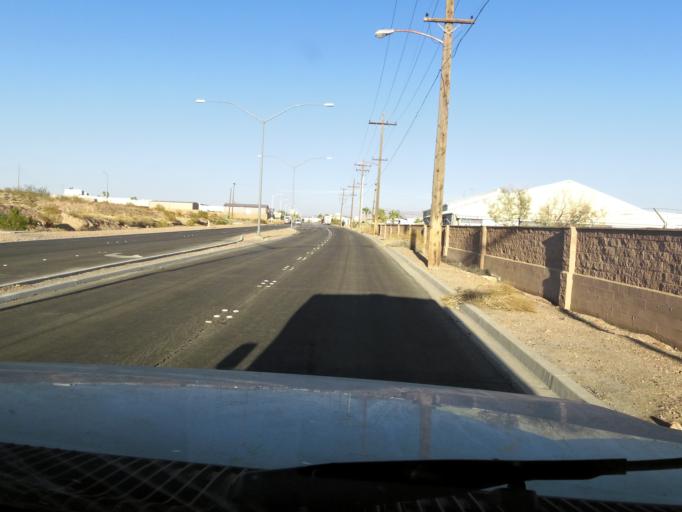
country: US
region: Nevada
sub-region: Clark County
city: Boulder City
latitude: 35.9731
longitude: -114.8584
